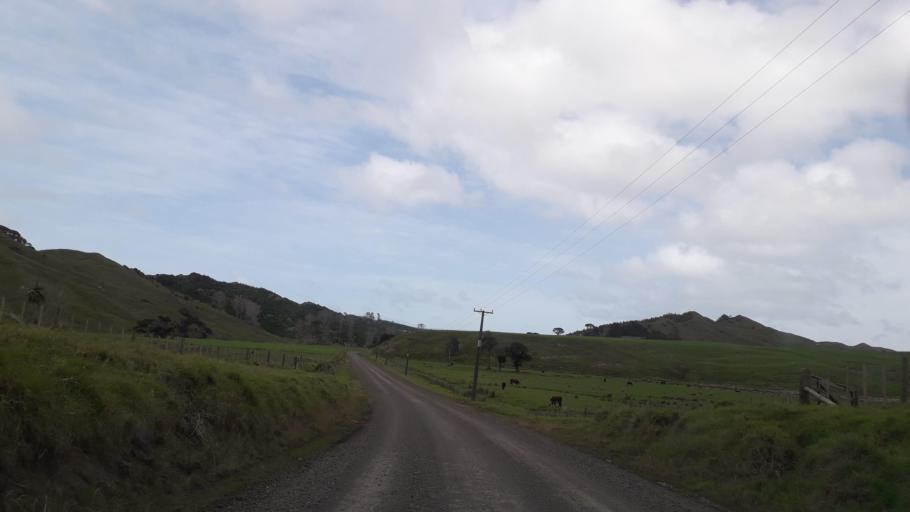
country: NZ
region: Northland
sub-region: Far North District
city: Ahipara
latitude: -35.4195
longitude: 173.3617
